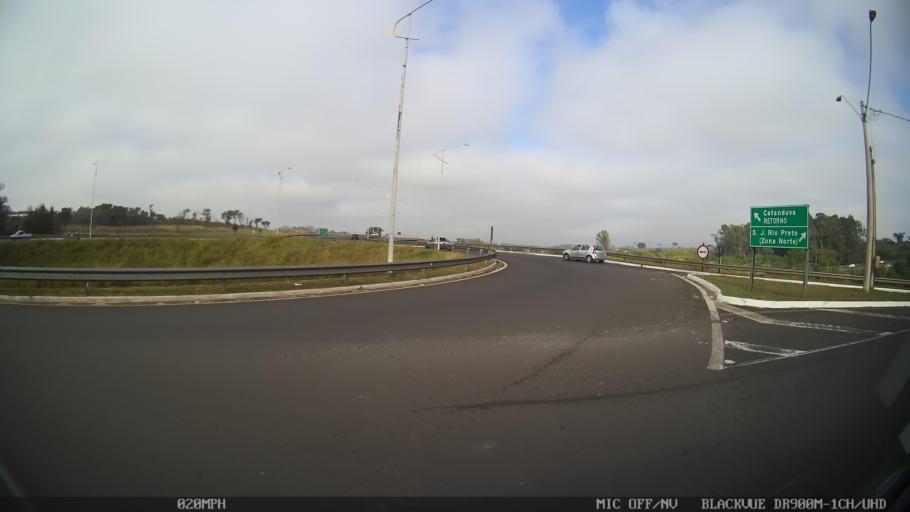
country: BR
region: Sao Paulo
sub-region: Sao Jose Do Rio Preto
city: Sao Jose do Rio Preto
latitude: -20.8170
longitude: -49.4341
